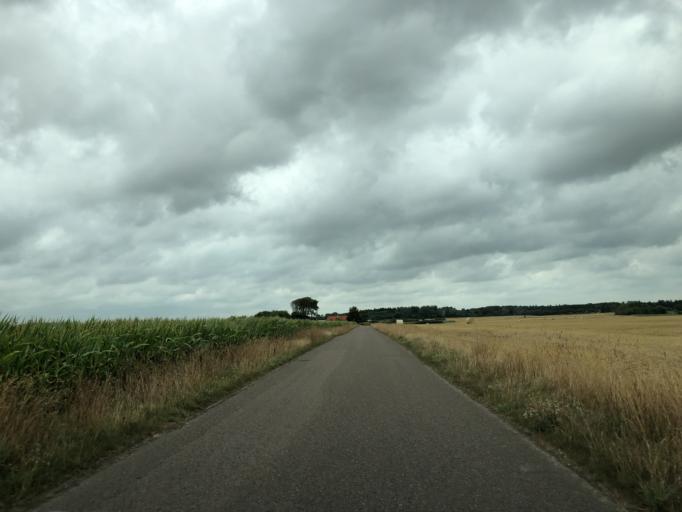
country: DK
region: Central Jutland
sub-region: Ringkobing-Skjern Kommune
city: Skjern
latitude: 56.0939
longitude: 8.4814
